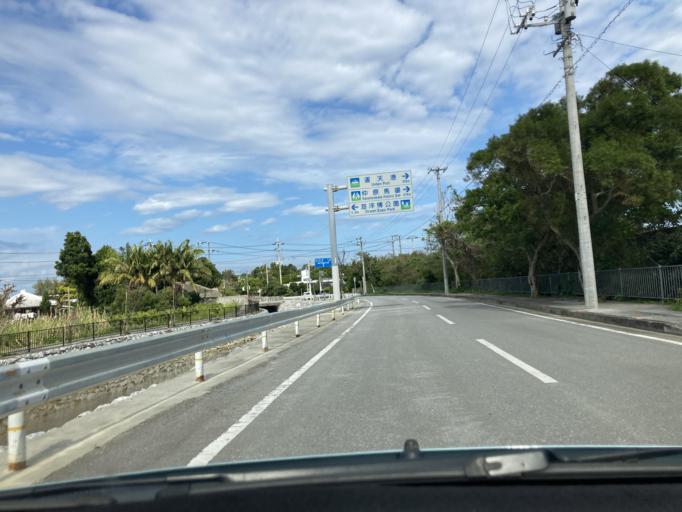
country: JP
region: Okinawa
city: Nago
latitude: 26.7003
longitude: 127.9252
